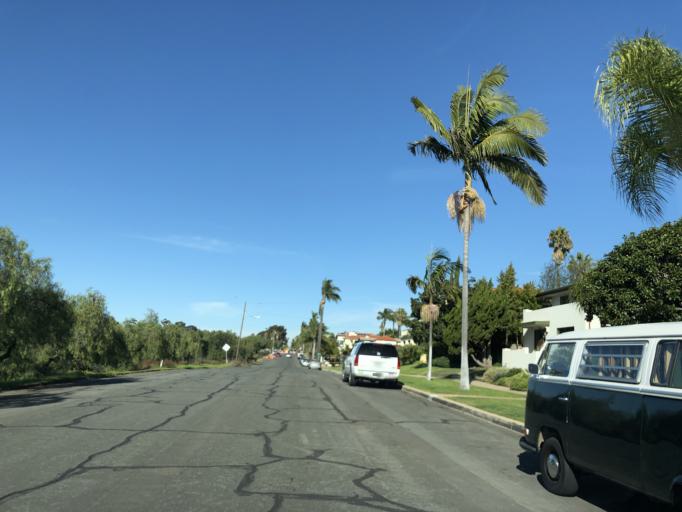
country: US
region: California
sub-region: San Diego County
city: San Diego
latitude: 32.7347
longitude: -117.1336
